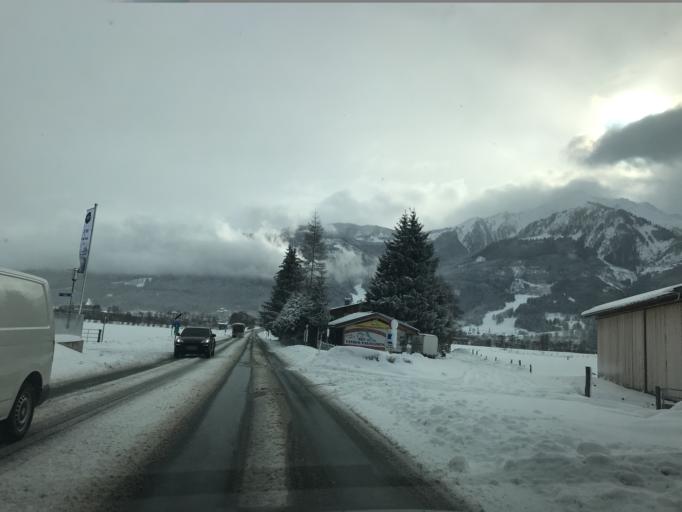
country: AT
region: Salzburg
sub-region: Politischer Bezirk Zell am See
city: Kaprun
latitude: 47.2877
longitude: 12.7469
